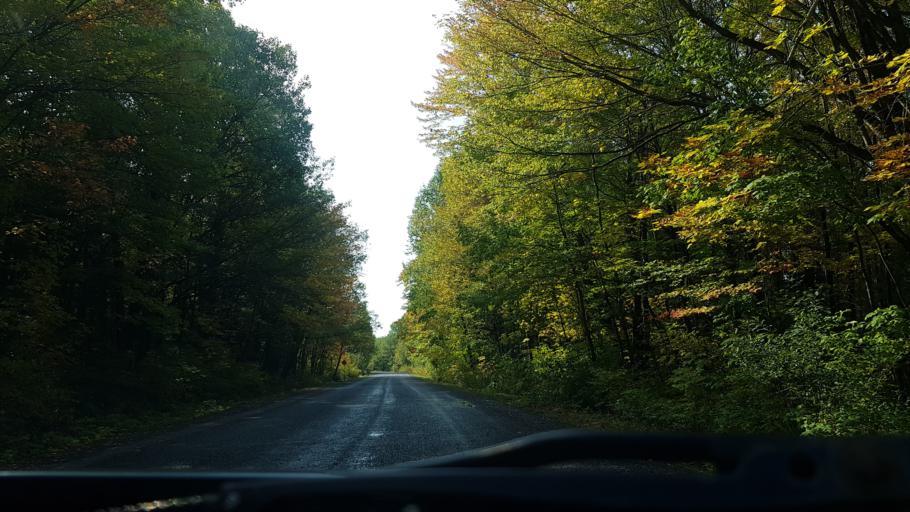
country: CA
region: Ontario
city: Gravenhurst
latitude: 44.8340
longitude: -79.2162
